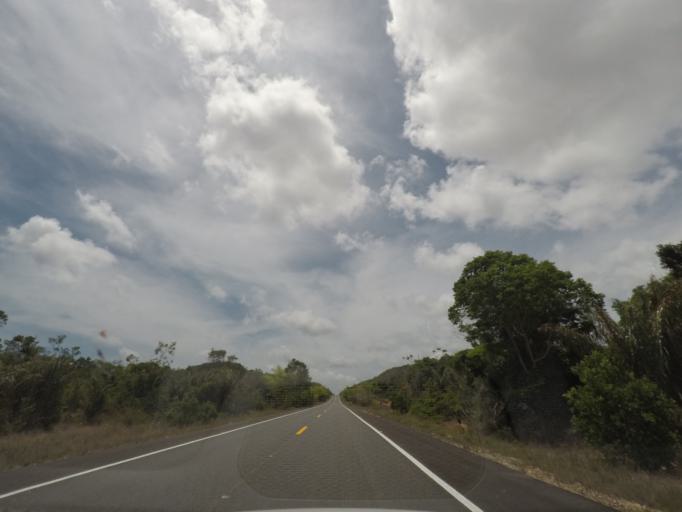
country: BR
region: Bahia
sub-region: Conde
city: Conde
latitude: -11.6784
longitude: -37.5640
